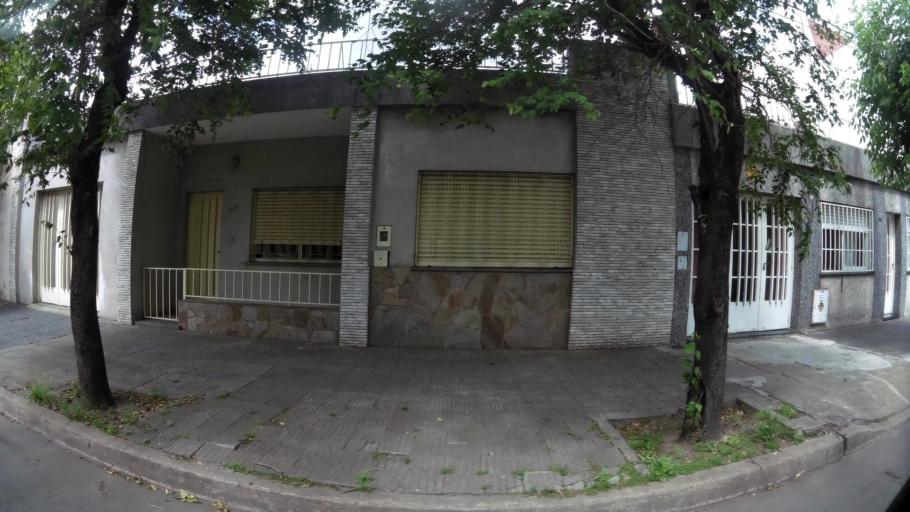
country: AR
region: Santa Fe
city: Gobernador Galvez
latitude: -32.9970
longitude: -60.6320
